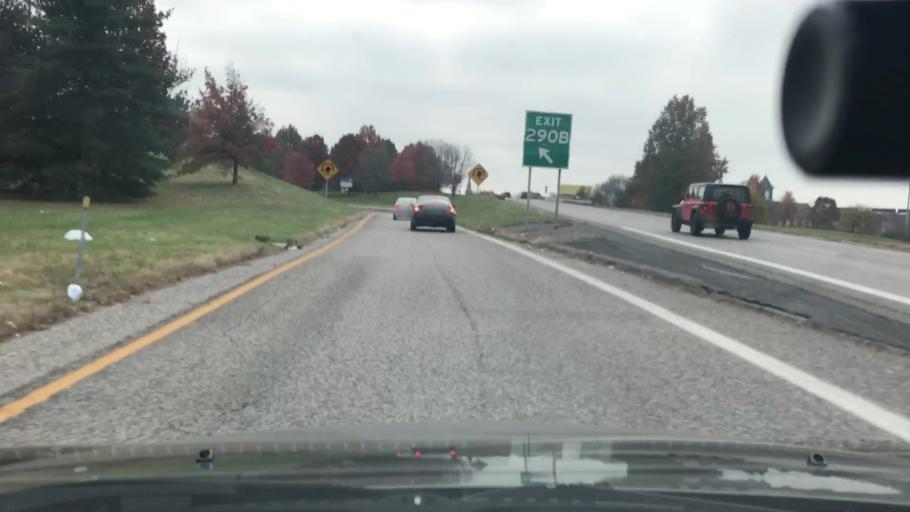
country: US
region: Missouri
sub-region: City of Saint Louis
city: St. Louis
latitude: 38.6117
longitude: -90.2136
